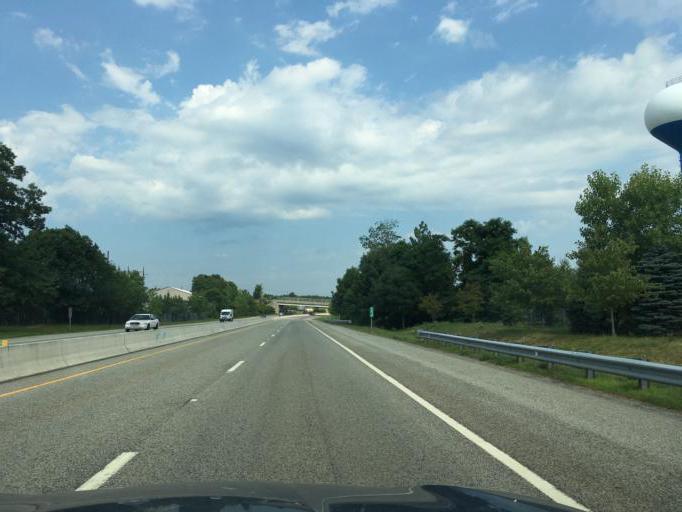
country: US
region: Rhode Island
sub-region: Kent County
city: East Greenwich
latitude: 41.6073
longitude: -71.4681
